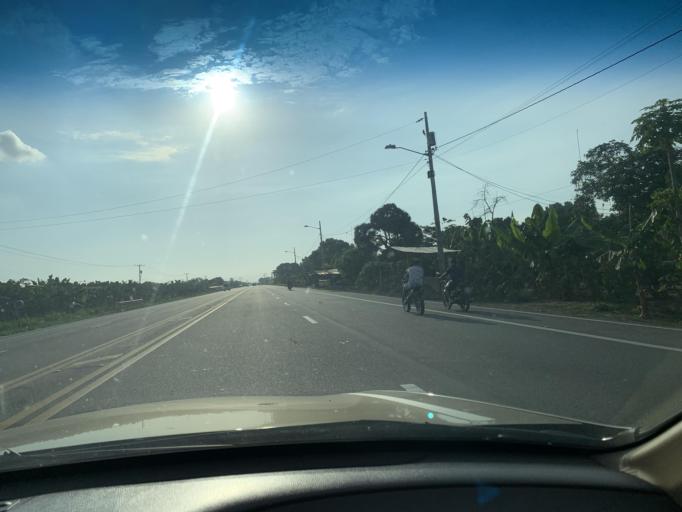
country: EC
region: Guayas
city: Naranjito
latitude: -2.2570
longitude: -79.5816
